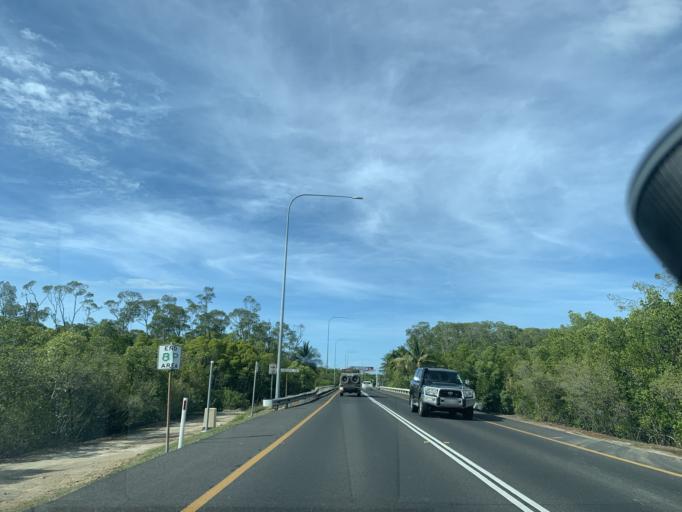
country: AU
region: Queensland
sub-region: Cairns
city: Cairns
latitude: -16.8924
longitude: 145.7605
